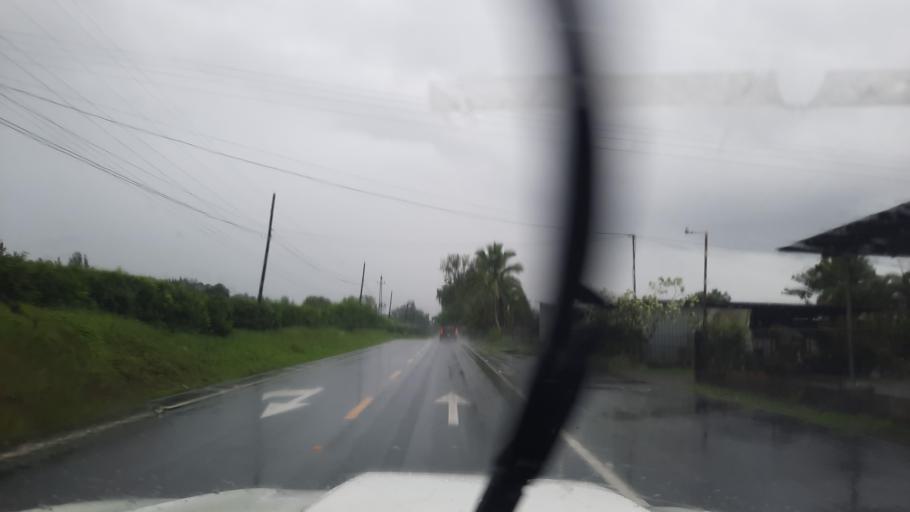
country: PA
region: Chiriqui
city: Sortova
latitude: 8.5701
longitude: -82.6328
